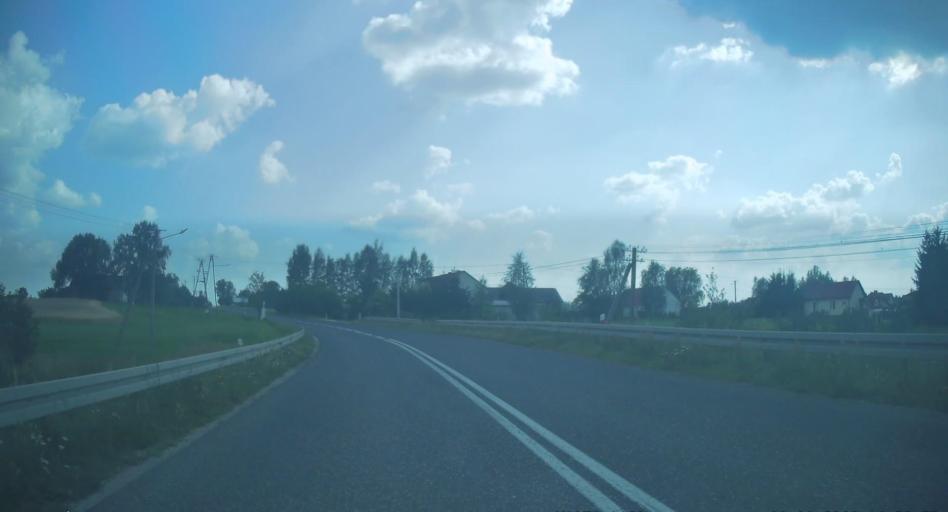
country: PL
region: Swietokrzyskie
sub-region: Powiat kielecki
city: Lopuszno
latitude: 50.9100
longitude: 20.2451
